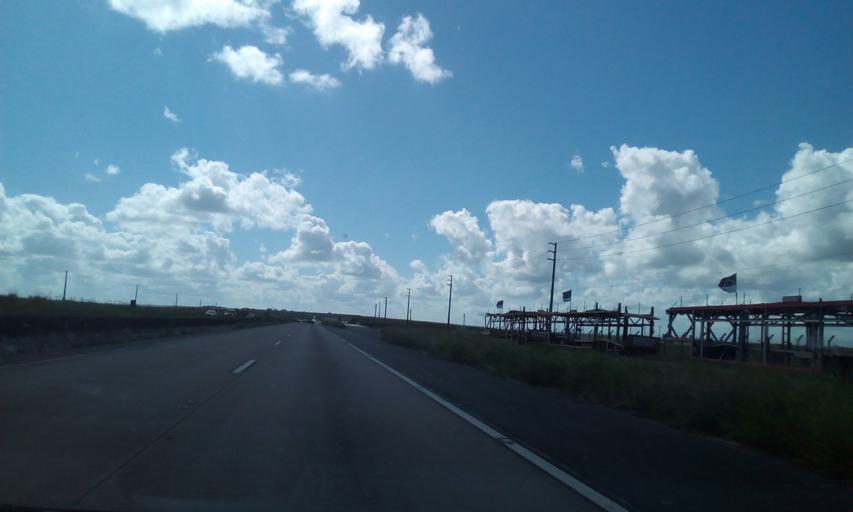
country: BR
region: Pernambuco
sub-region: Goiana
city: Goiana
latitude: -7.6185
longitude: -34.9708
